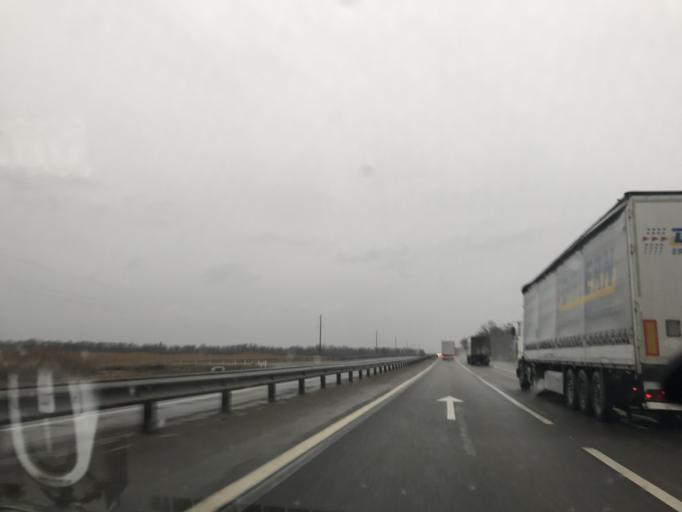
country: RU
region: Krasnodarskiy
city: Kislyakovskaya
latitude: 46.3885
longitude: 39.7394
